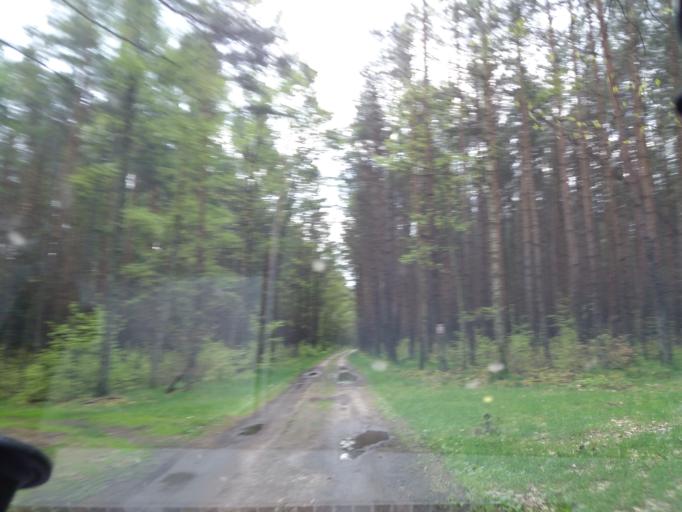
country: PL
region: West Pomeranian Voivodeship
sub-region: Powiat choszczenski
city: Drawno
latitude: 53.1164
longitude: 15.8631
